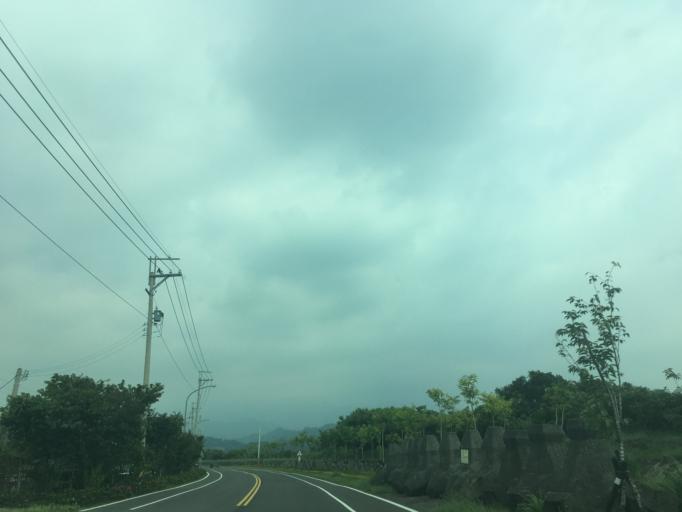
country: TW
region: Taiwan
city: Fengyuan
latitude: 24.2914
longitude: 120.8406
